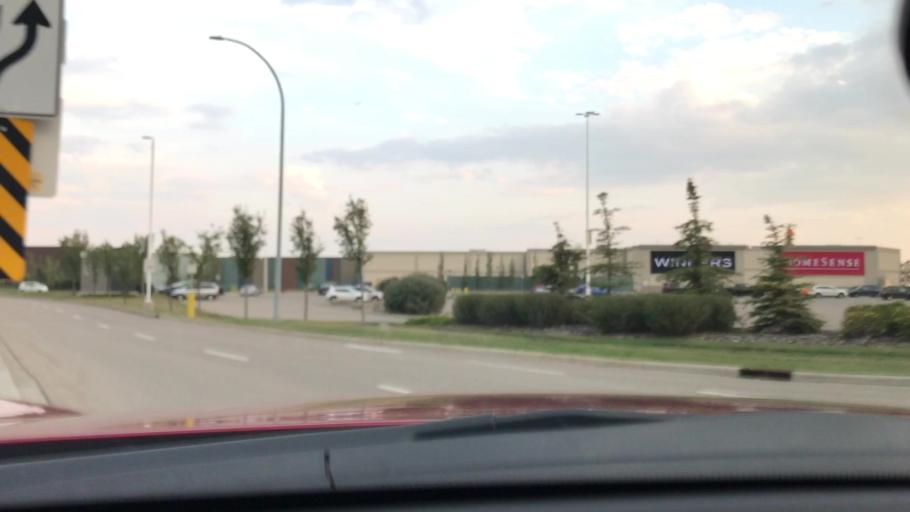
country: CA
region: Alberta
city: Airdrie
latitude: 51.2073
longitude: -113.9939
